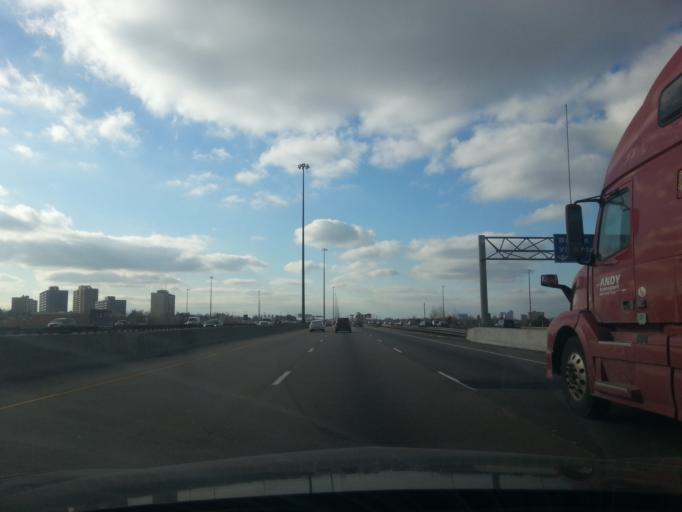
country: CA
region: Ontario
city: Scarborough
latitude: 43.7762
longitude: -79.2795
